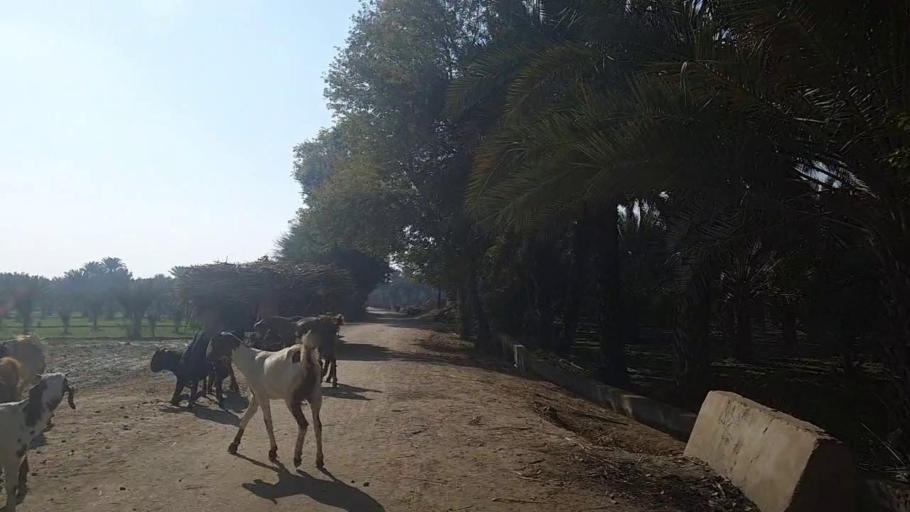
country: PK
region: Sindh
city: Khairpur
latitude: 27.4441
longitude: 68.7384
